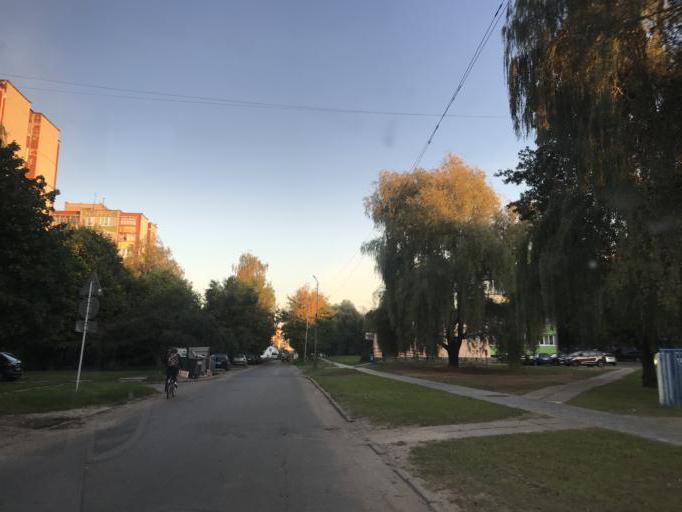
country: BY
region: Mogilev
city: Mahilyow
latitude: 53.9071
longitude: 30.3200
